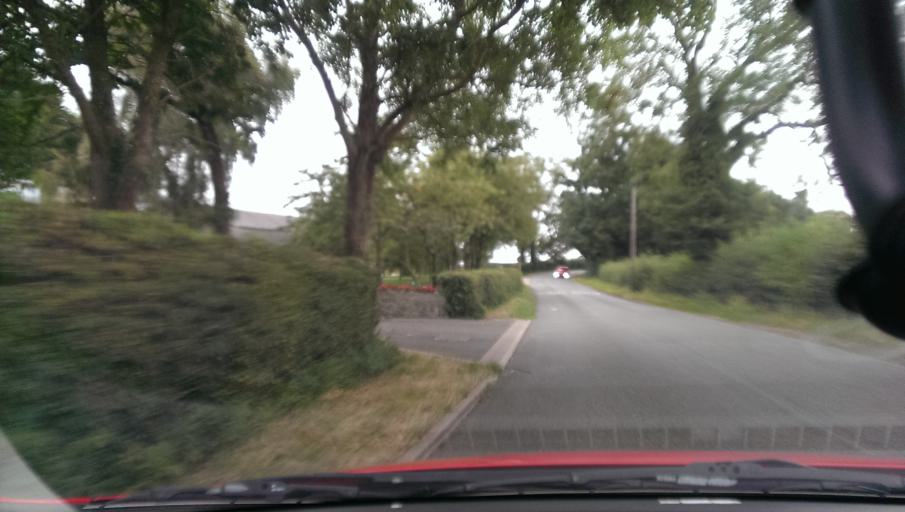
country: GB
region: England
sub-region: Leicestershire
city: Great Glen
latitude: 52.5677
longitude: -1.0547
